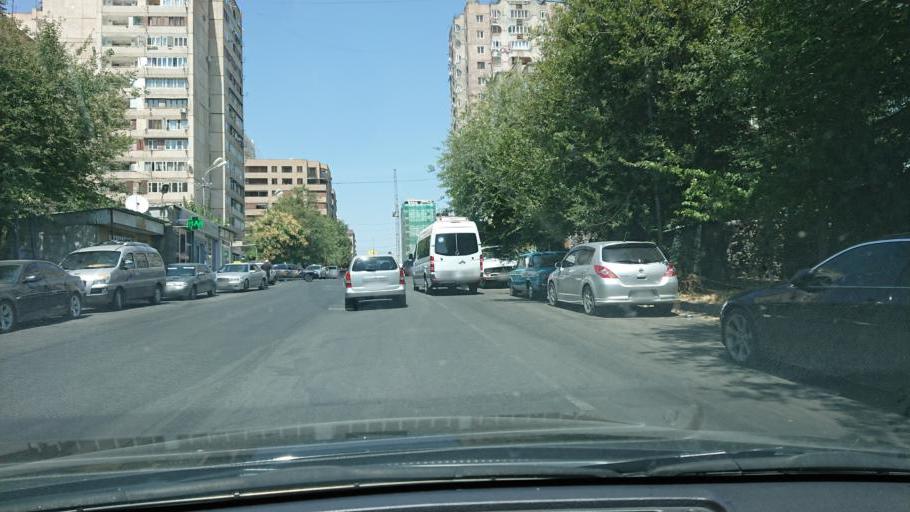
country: AM
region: Yerevan
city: Yerevan
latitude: 40.1975
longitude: 44.5025
